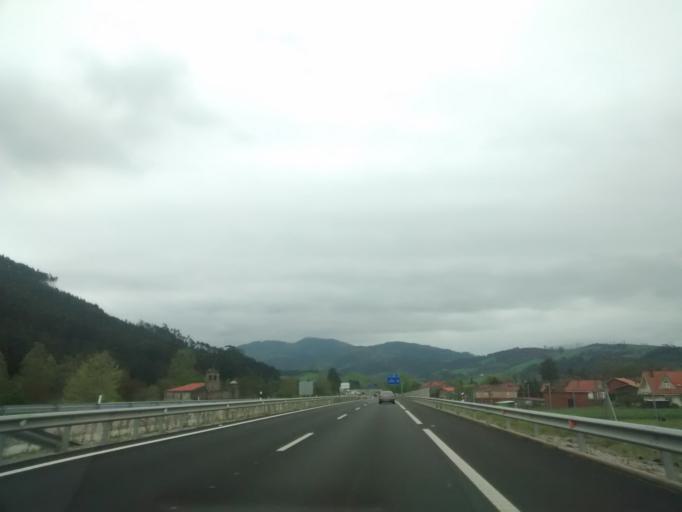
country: ES
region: Cantabria
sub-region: Provincia de Cantabria
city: Puente Viesgo
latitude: 43.3277
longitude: -3.9620
